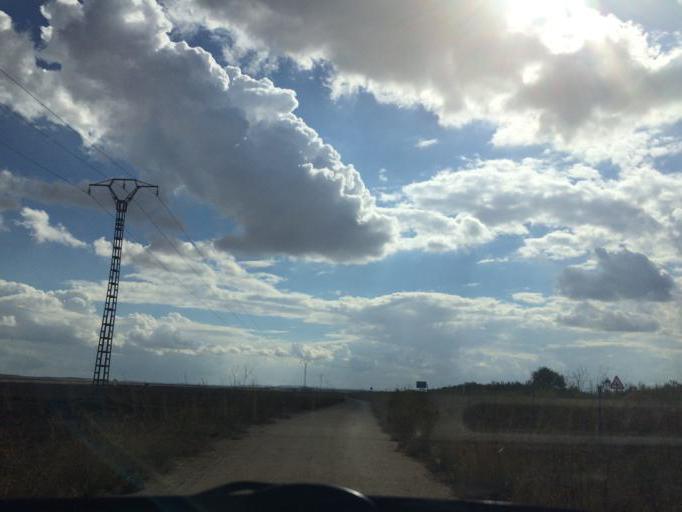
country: ES
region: Castille-La Mancha
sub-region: Provincia de Albacete
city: Albacete
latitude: 38.9561
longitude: -1.8218
